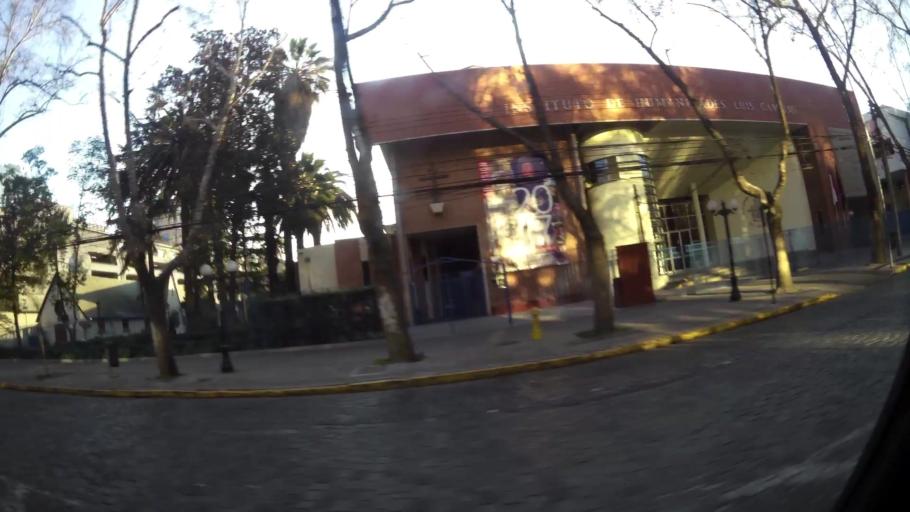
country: CL
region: Santiago Metropolitan
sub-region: Provincia de Santiago
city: Villa Presidente Frei, Nunoa, Santiago, Chile
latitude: -33.4261
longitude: -70.6113
